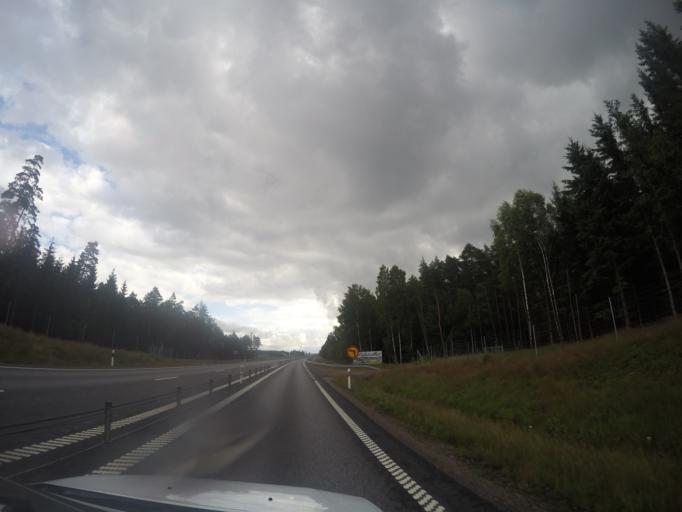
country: SE
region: Kronoberg
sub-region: Ljungby Kommun
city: Ljungby
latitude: 56.8077
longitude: 13.8864
